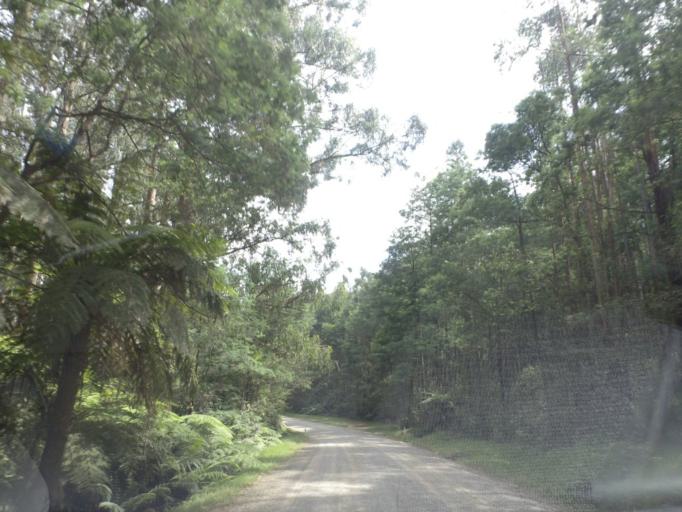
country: AU
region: Victoria
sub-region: Yarra Ranges
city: Healesville
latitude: -37.5488
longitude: 145.5151
